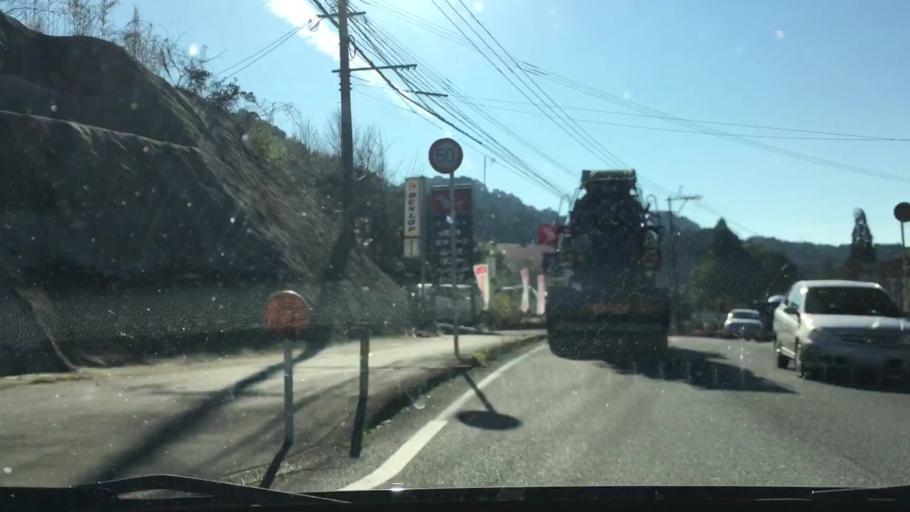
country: JP
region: Kagoshima
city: Kajiki
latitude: 31.7551
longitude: 130.6781
